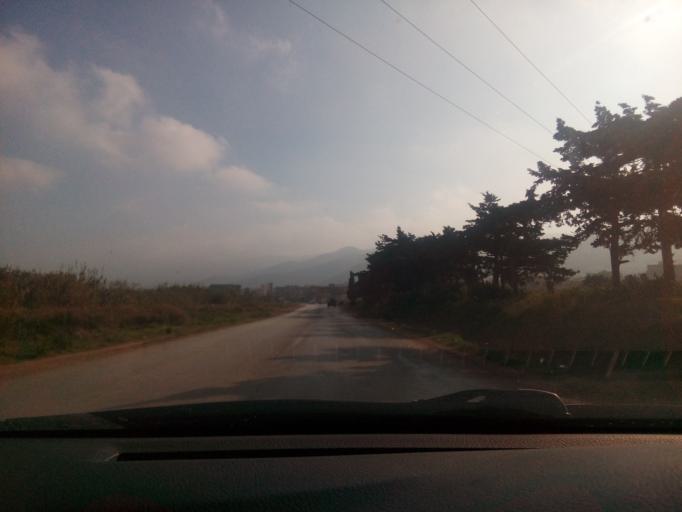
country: DZ
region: Oran
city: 'Ain el Turk
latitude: 35.7038
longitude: -0.8239
